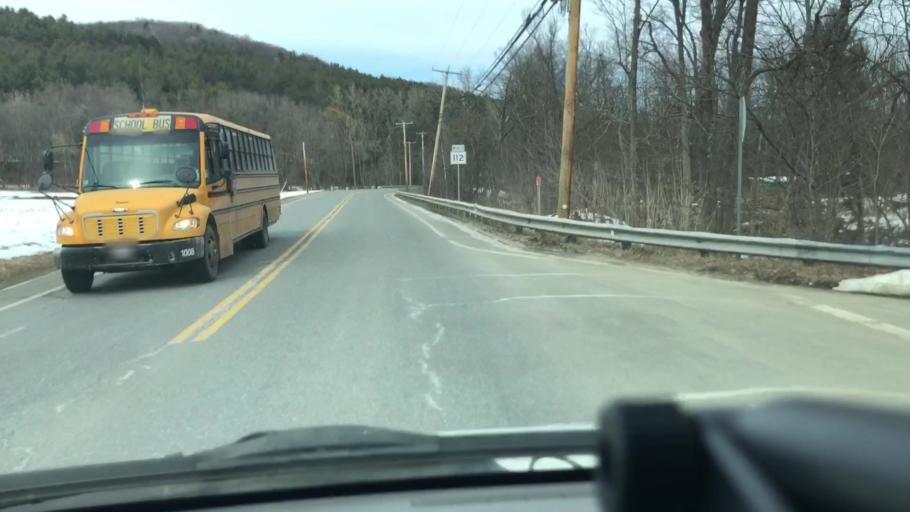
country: US
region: Massachusetts
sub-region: Franklin County
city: Buckland
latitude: 42.5917
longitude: -72.7867
